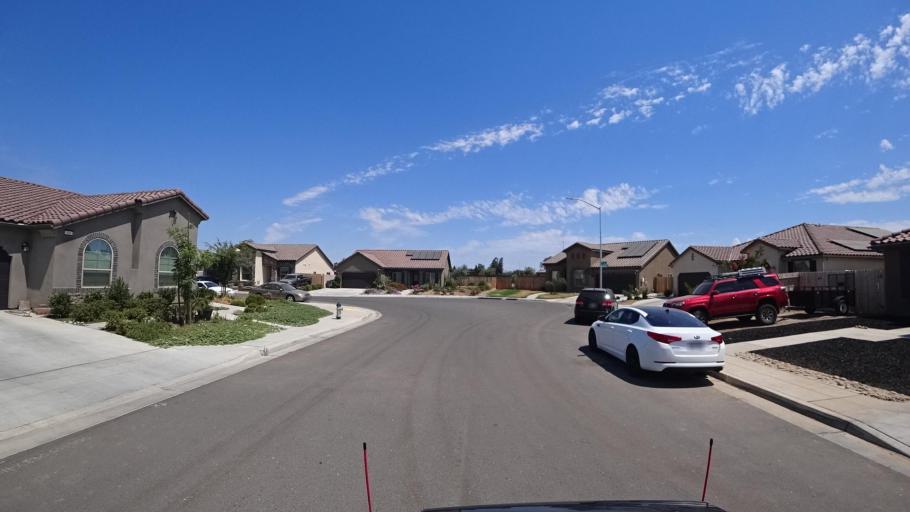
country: US
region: California
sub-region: Fresno County
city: Sunnyside
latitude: 36.7328
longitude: -119.7119
